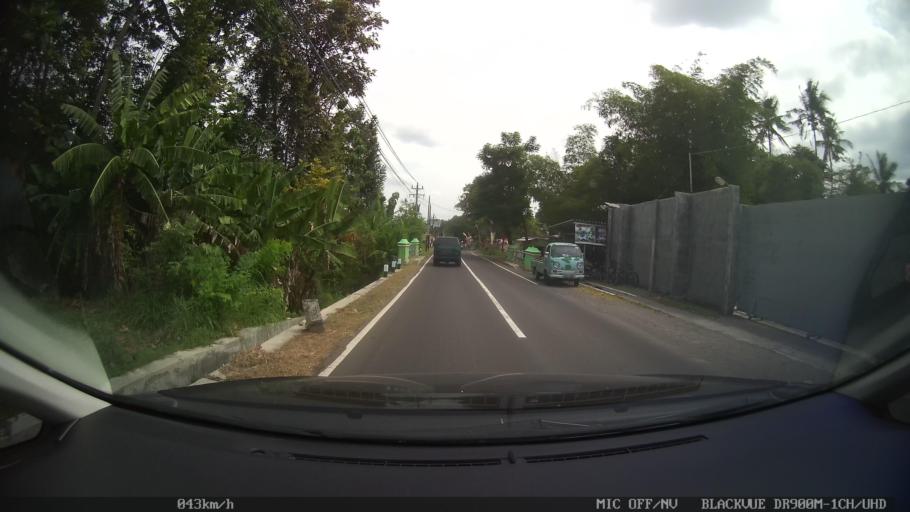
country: ID
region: Central Java
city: Candi Prambanan
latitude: -7.7301
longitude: 110.4638
